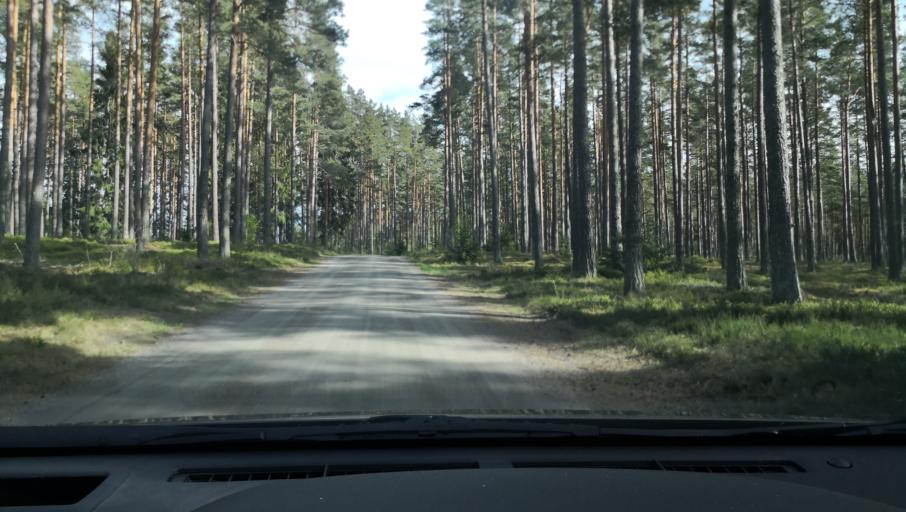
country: SE
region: OErebro
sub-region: Askersunds Kommun
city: Asbro
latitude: 59.0348
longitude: 15.0414
